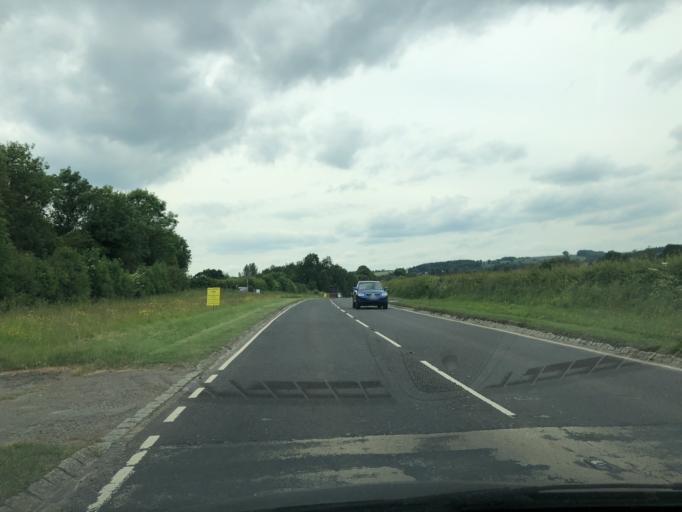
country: GB
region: England
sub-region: North Yorkshire
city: Helmsley
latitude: 54.2471
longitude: -1.0459
